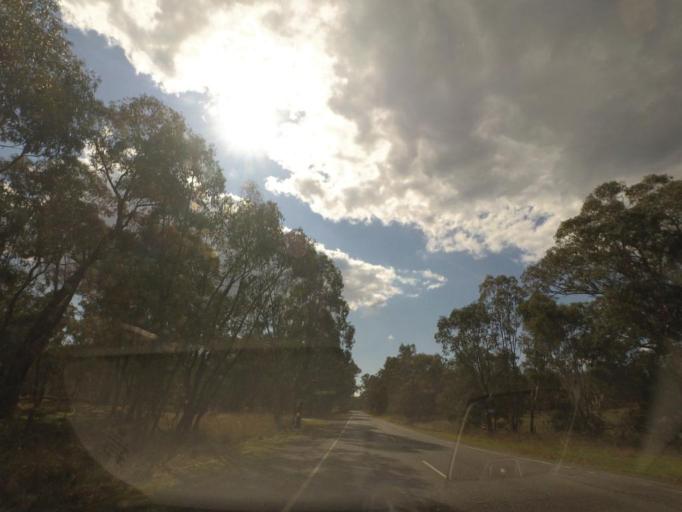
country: AU
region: New South Wales
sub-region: Corowa Shire
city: Howlong
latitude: -36.1767
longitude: 146.6074
